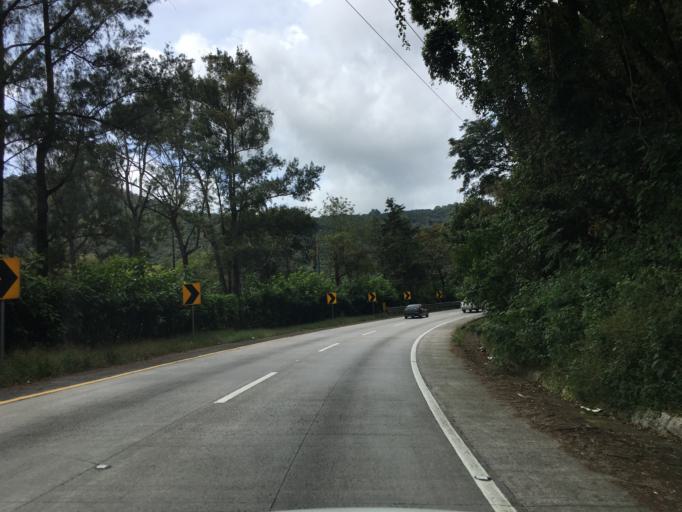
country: GT
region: Sacatepequez
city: Santa Lucia Milpas Altas
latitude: 14.5628
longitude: -90.6999
